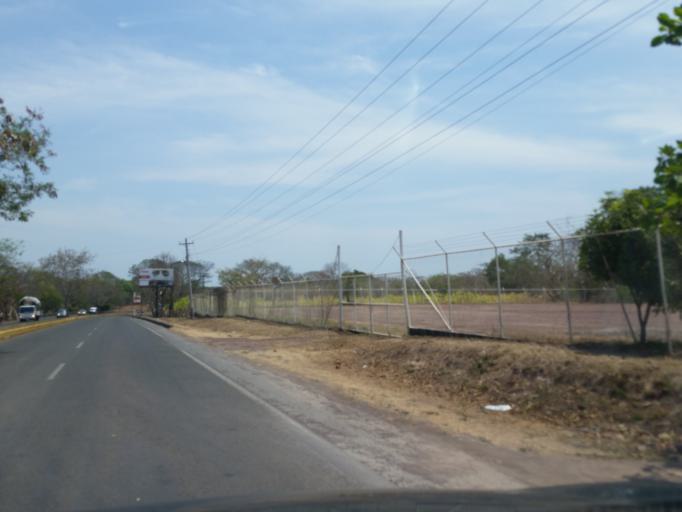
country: NI
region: Granada
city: Granada
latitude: 11.9618
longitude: -85.9982
